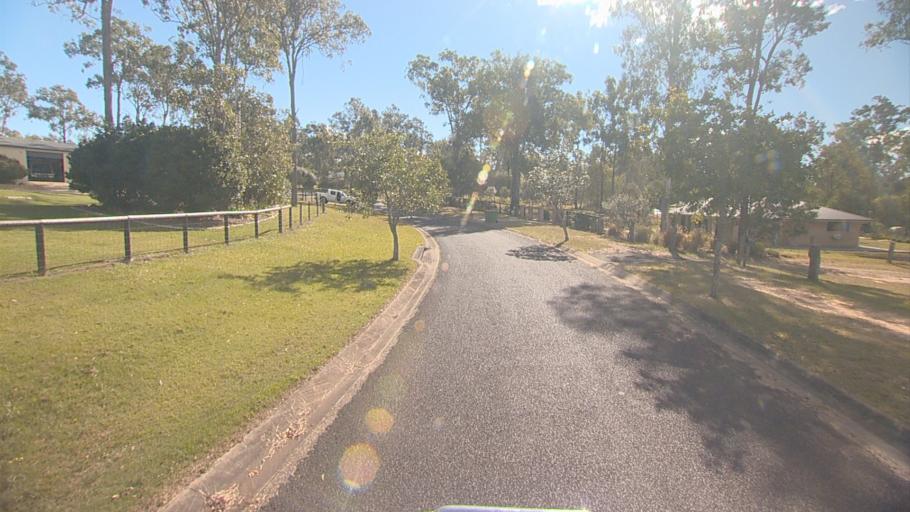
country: AU
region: Queensland
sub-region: Logan
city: North Maclean
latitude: -27.7481
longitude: 152.9380
